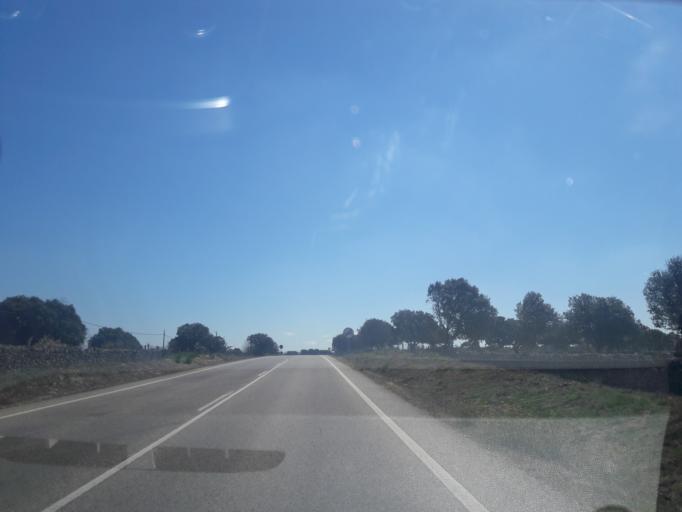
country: ES
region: Castille and Leon
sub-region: Provincia de Salamanca
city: Encina de San Silvestre
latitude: 41.0367
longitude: -6.0641
